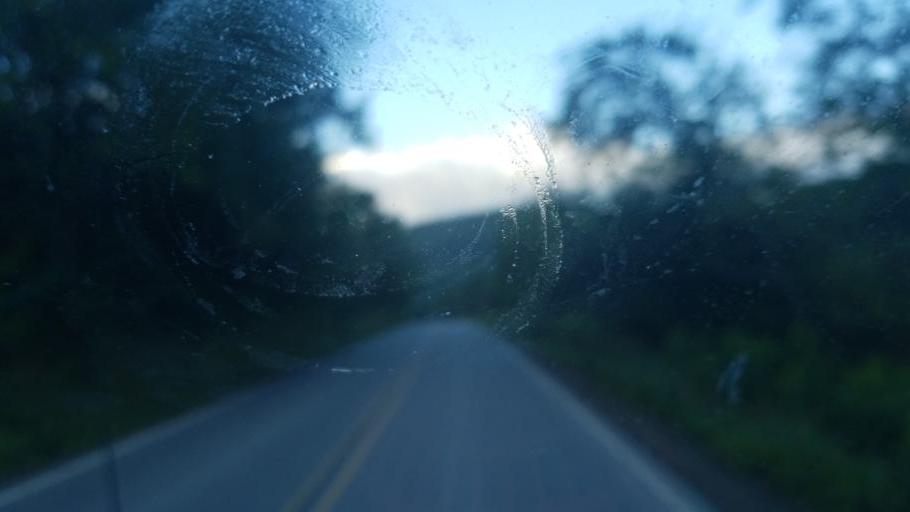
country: US
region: Pennsylvania
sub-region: Potter County
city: Galeton
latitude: 41.8399
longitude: -77.7887
